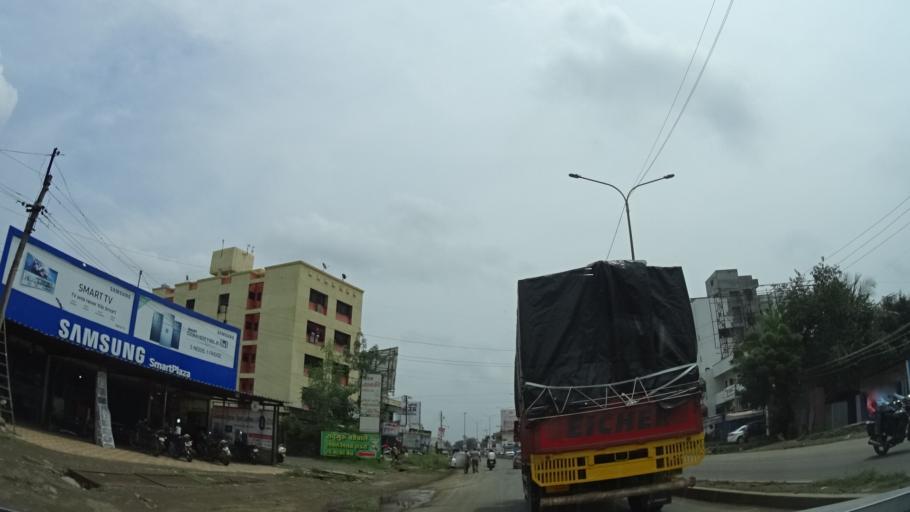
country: IN
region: Maharashtra
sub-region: Pune Division
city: Koregaon
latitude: 18.6457
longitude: 74.0621
